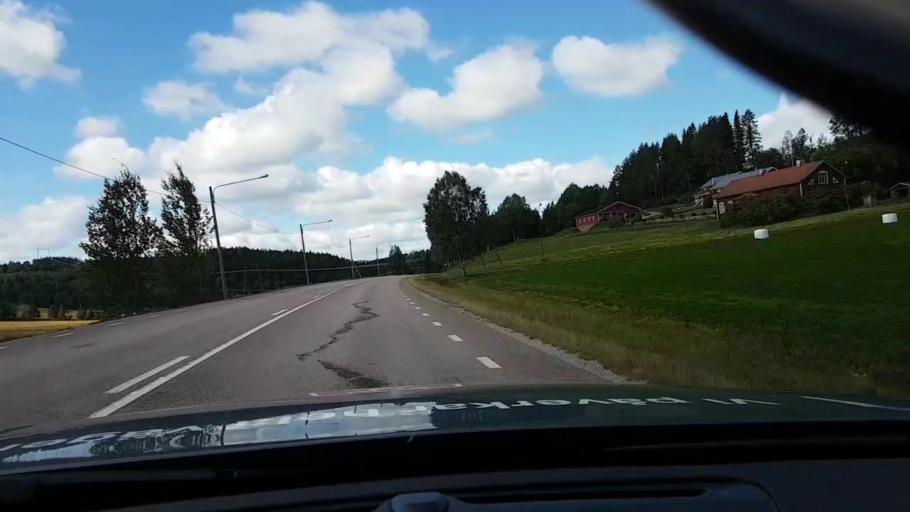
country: SE
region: Vaesternorrland
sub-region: OErnskoeldsviks Kommun
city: Bjasta
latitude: 63.3859
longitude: 18.3773
